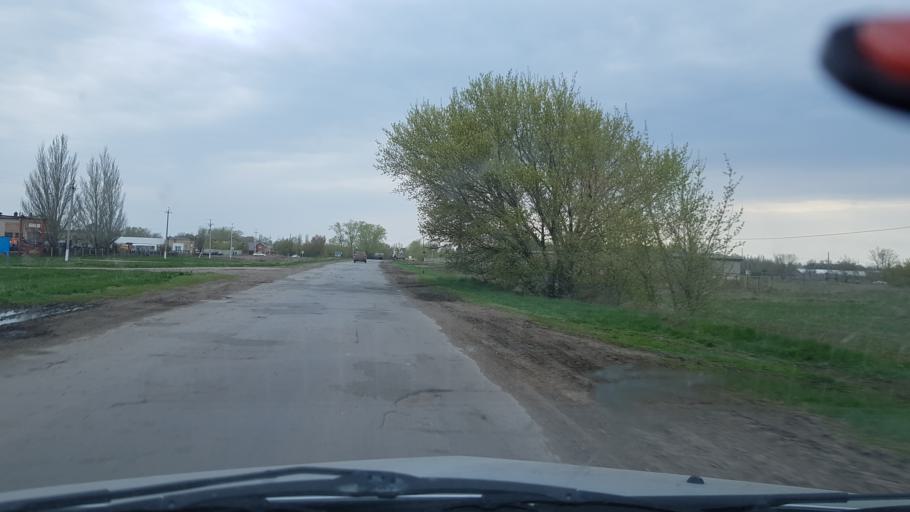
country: RU
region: Samara
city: Khryashchevka
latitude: 53.6727
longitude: 49.0826
